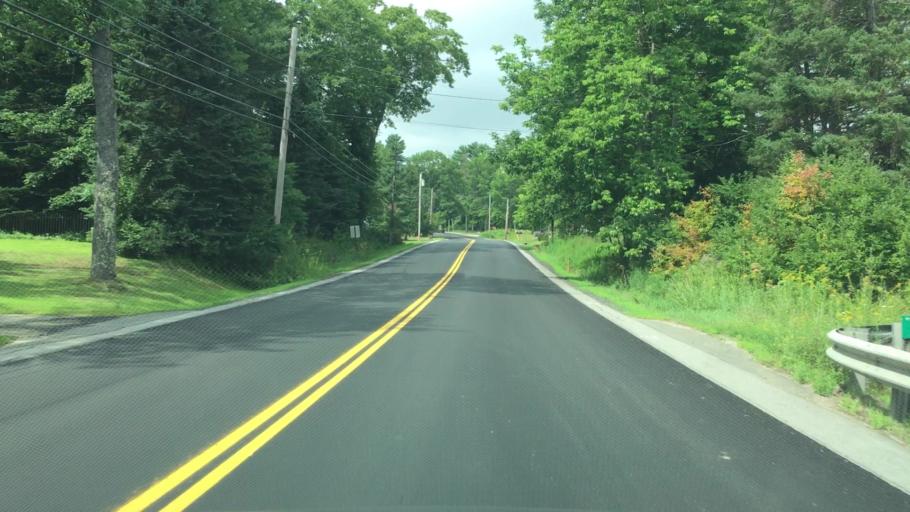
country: US
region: Maine
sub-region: Hancock County
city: Bucksport
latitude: 44.6021
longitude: -68.8163
